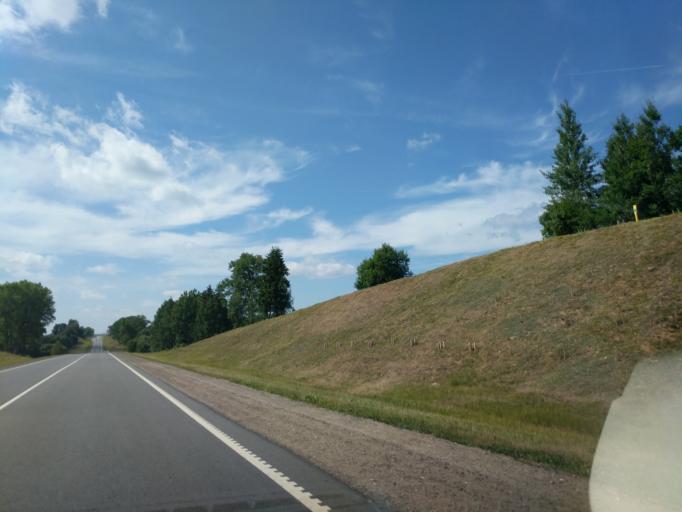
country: BY
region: Minsk
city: Syomkava
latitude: 54.1036
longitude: 27.4743
